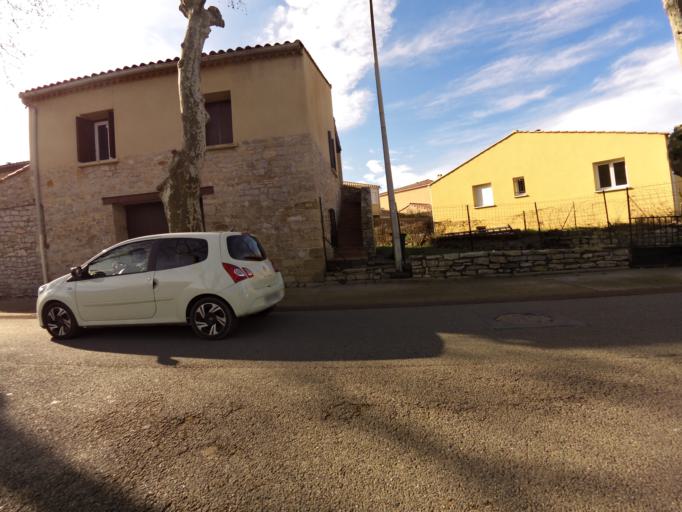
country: FR
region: Languedoc-Roussillon
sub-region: Departement de l'Herault
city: Saint-Martin-de-Londres
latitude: 43.7879
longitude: 3.7328
